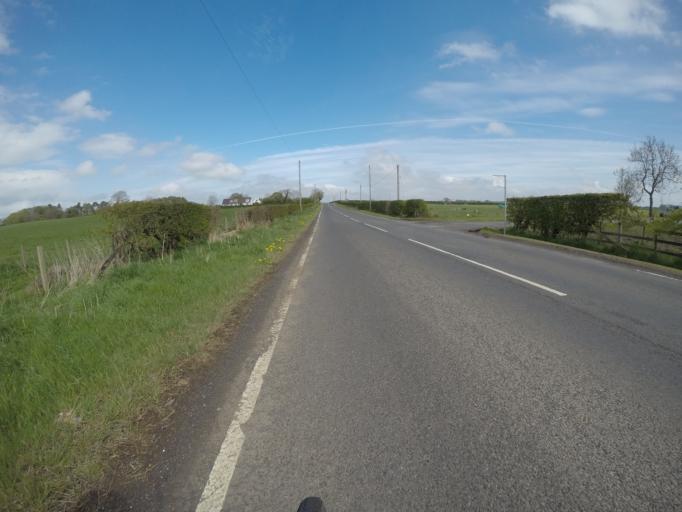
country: GB
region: Scotland
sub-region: East Ayrshire
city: Kilmaurs
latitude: 55.6604
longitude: -4.5501
